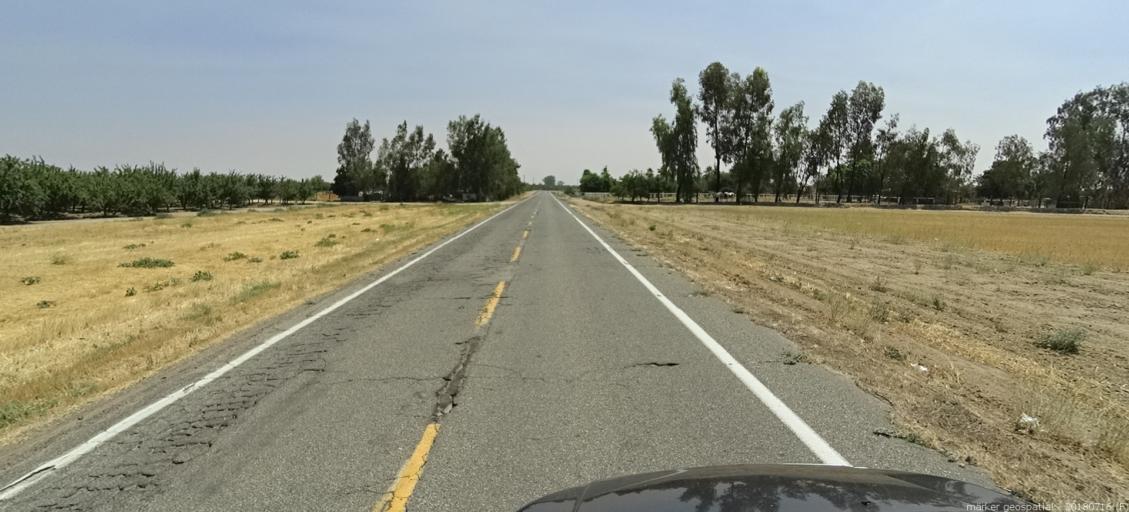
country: US
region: California
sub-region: Madera County
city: Madera Acres
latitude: 37.0527
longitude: -120.0937
